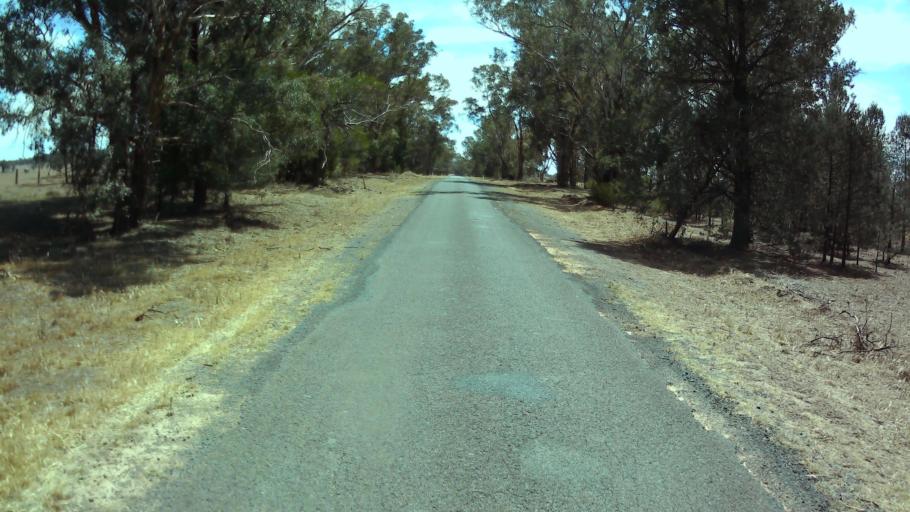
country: AU
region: New South Wales
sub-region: Weddin
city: Grenfell
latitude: -33.7566
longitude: 148.2059
